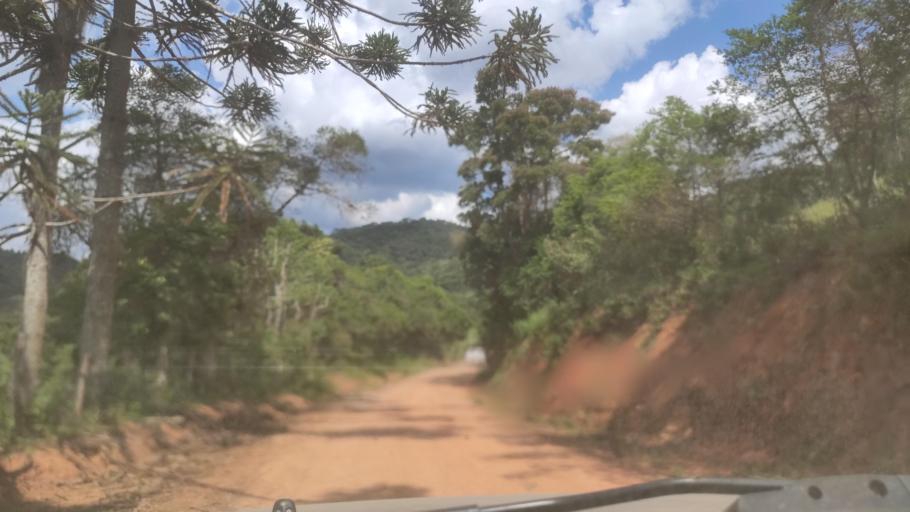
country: BR
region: Minas Gerais
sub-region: Camanducaia
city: Camanducaia
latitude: -22.7675
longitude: -45.9828
